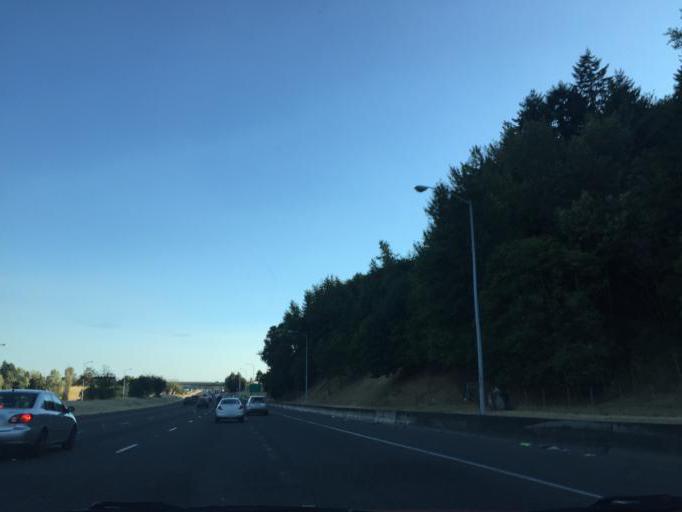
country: US
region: Oregon
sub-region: Multnomah County
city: Lents
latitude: 45.5408
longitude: -122.5629
